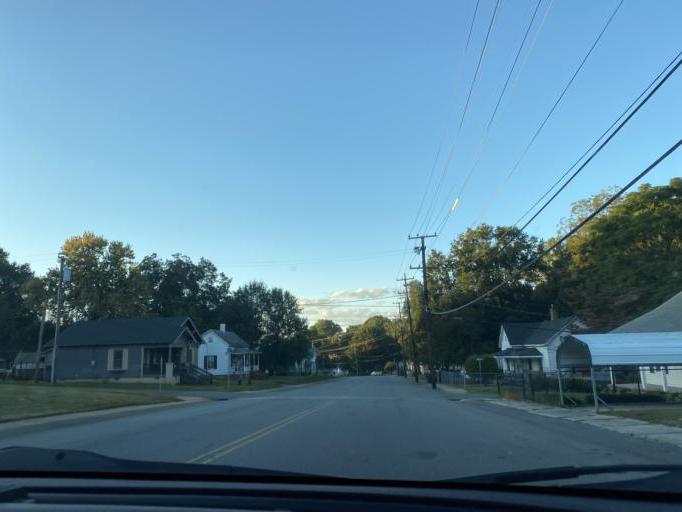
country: US
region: South Carolina
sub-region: Cherokee County
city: East Gaffney
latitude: 35.0802
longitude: -81.6378
